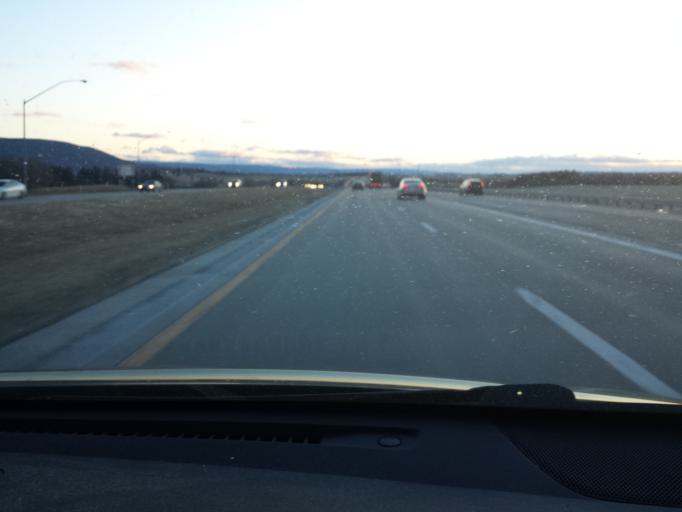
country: US
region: Pennsylvania
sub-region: Centre County
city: Pleasant Gap
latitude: 40.8704
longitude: -77.7814
